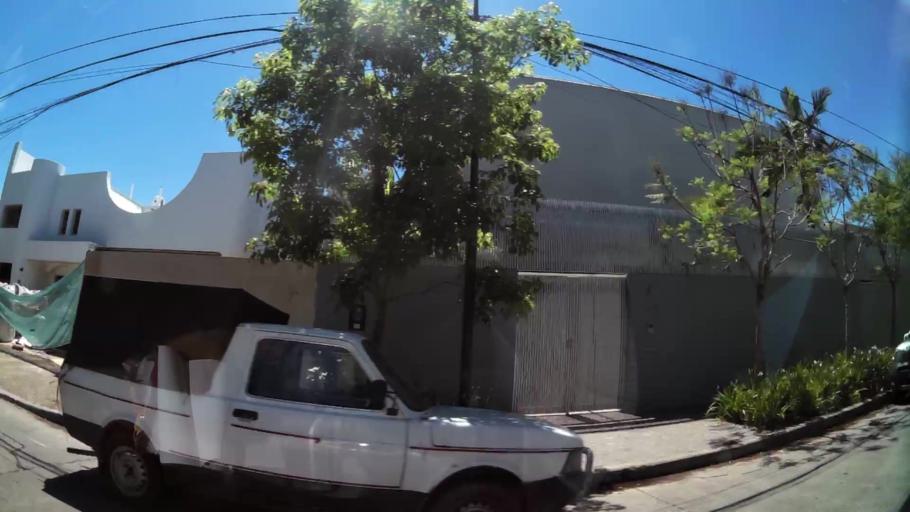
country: AR
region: Buenos Aires
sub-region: Partido de San Isidro
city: San Isidro
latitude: -34.4551
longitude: -58.5154
